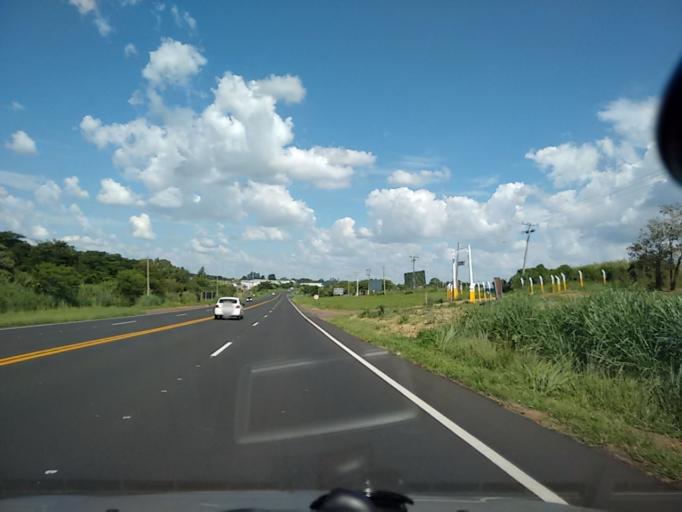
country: BR
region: Sao Paulo
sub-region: Pompeia
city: Pompeia
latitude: -22.1431
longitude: -50.1075
